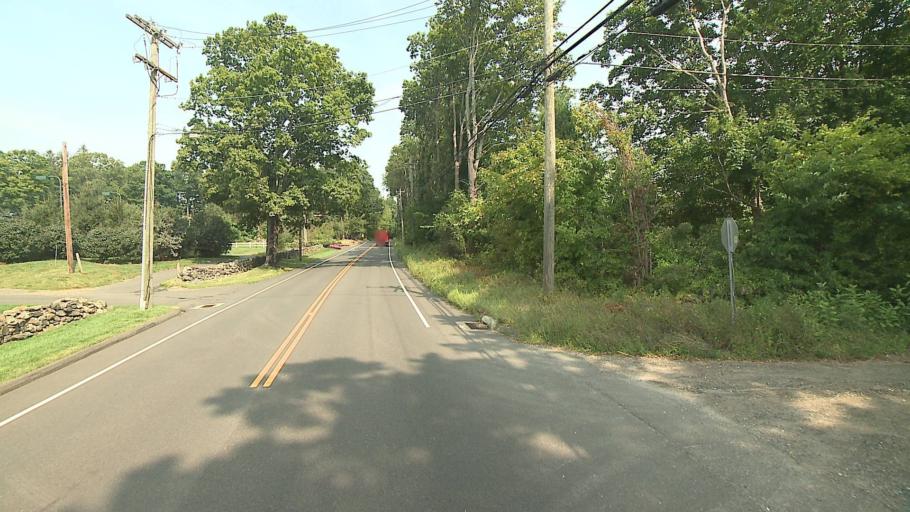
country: US
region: Connecticut
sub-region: Fairfield County
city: Bethel
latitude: 41.3221
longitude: -73.3867
